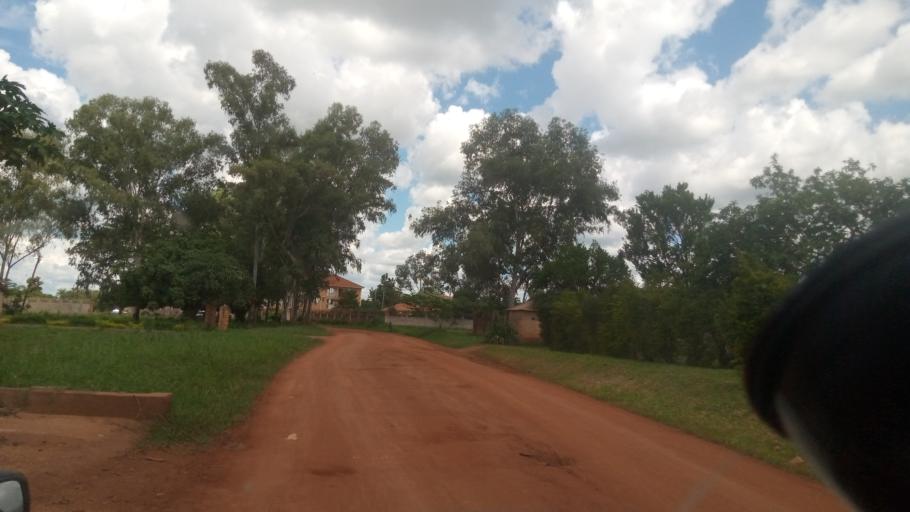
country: UG
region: Northern Region
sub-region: Lira District
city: Lira
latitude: 2.2391
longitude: 32.9048
